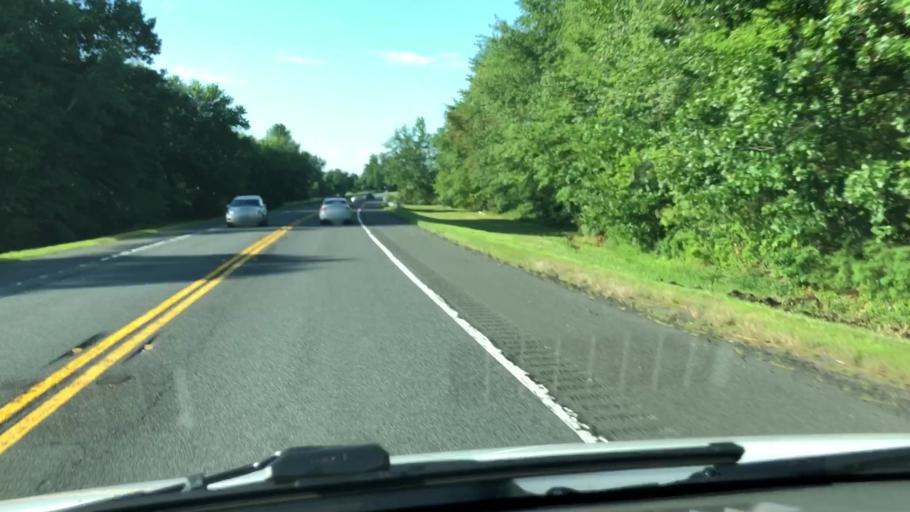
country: US
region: Massachusetts
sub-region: Hampshire County
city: North Amherst
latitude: 42.4197
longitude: -72.5369
